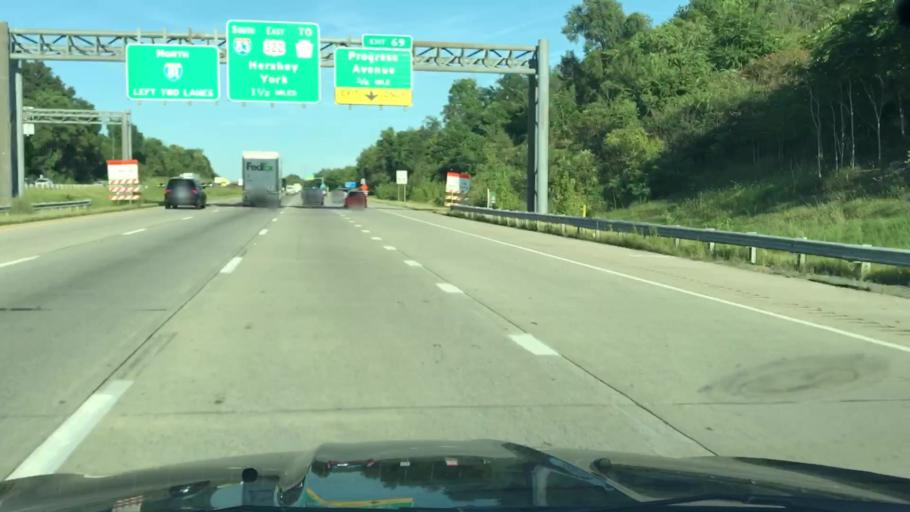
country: US
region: Pennsylvania
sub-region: Dauphin County
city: Harrisburg
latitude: 40.3011
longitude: -76.8692
